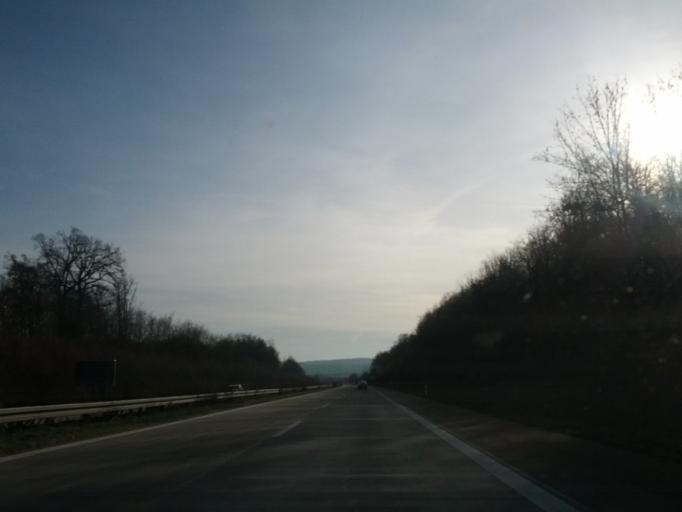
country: DE
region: Bavaria
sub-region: Regierungsbezirk Mittelfranken
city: Ohrenbach
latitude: 49.4692
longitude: 10.2319
